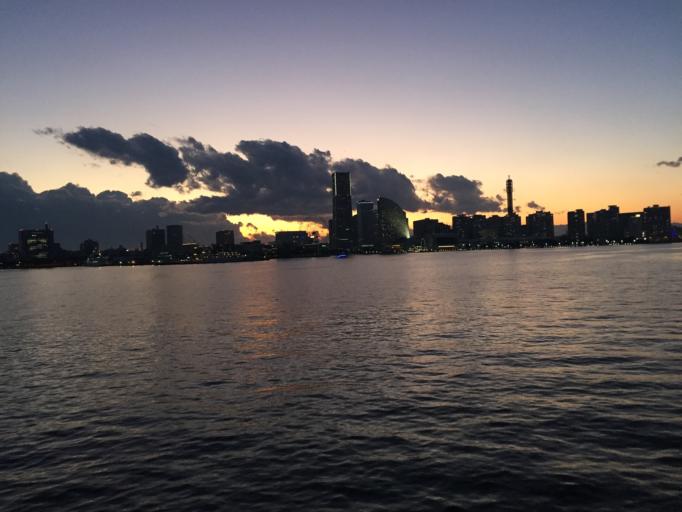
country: JP
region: Kanagawa
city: Yokohama
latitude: 35.4612
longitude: 139.6536
